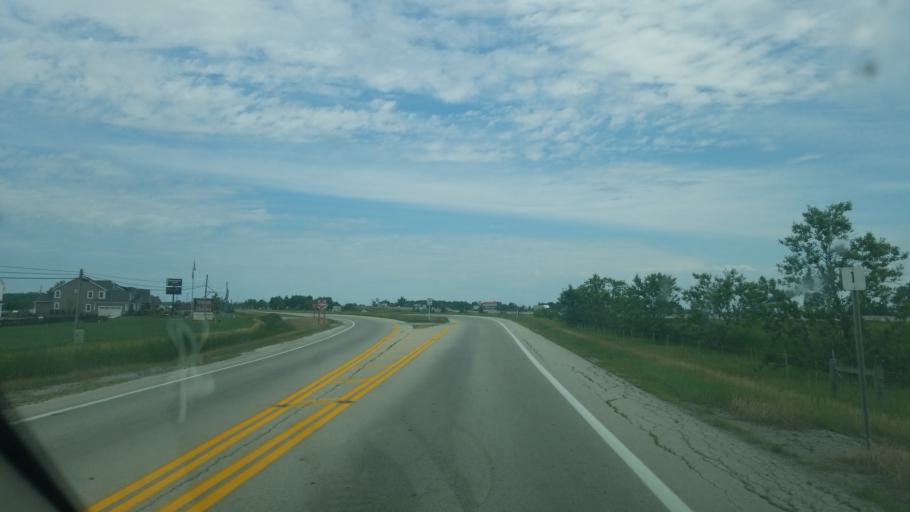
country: US
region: Ohio
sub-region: Wood County
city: North Baltimore
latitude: 41.2460
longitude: -83.6508
